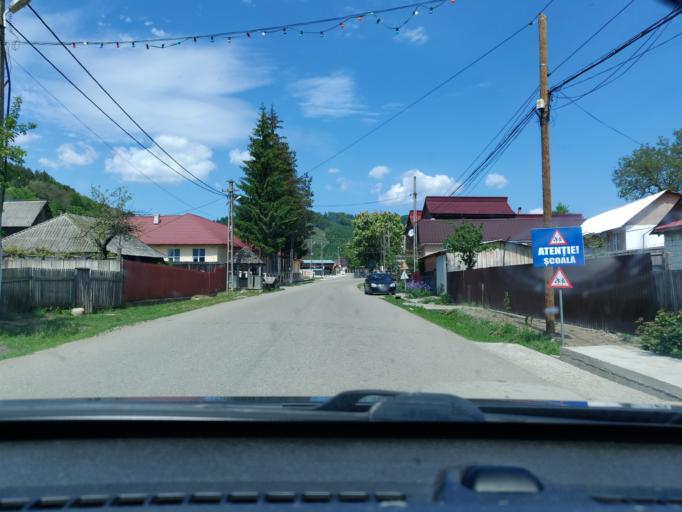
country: RO
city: Vizantea-Manastireasca
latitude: 45.9857
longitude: 26.7772
